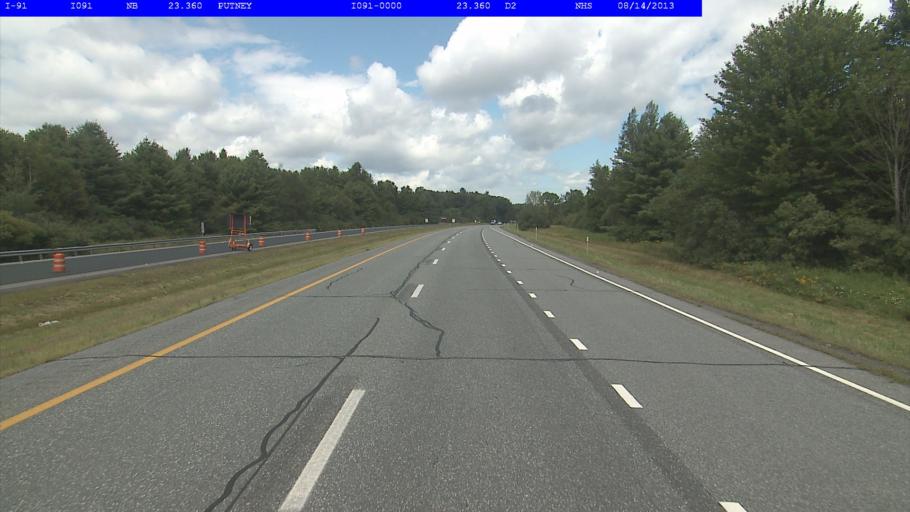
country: US
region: New Hampshire
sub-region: Cheshire County
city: Westmoreland
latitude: 43.0176
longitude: -72.4729
